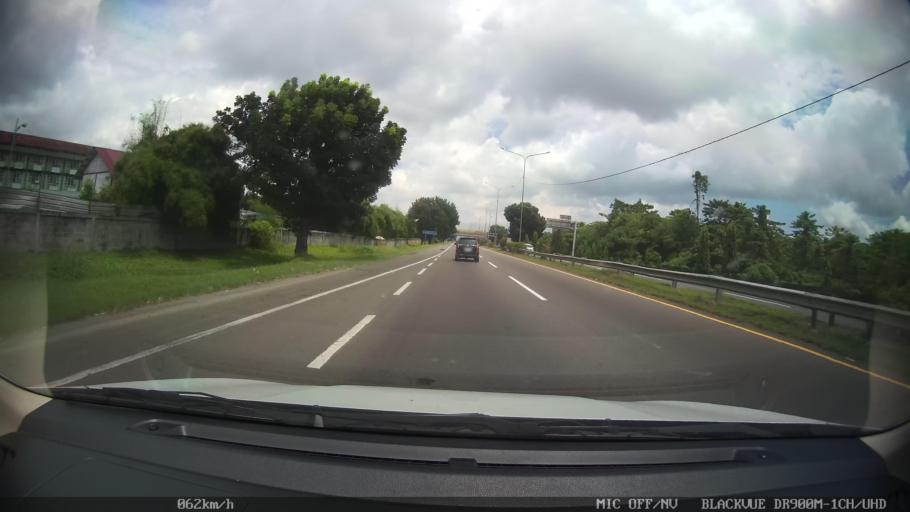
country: ID
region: North Sumatra
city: Medan
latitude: 3.6026
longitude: 98.7233
